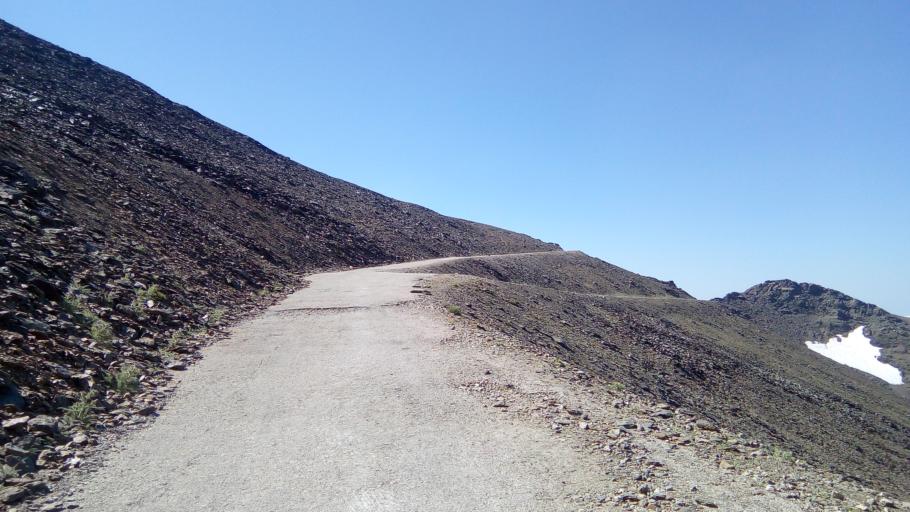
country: ES
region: Andalusia
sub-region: Provincia de Granada
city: Capileira
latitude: 37.0550
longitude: -3.3713
